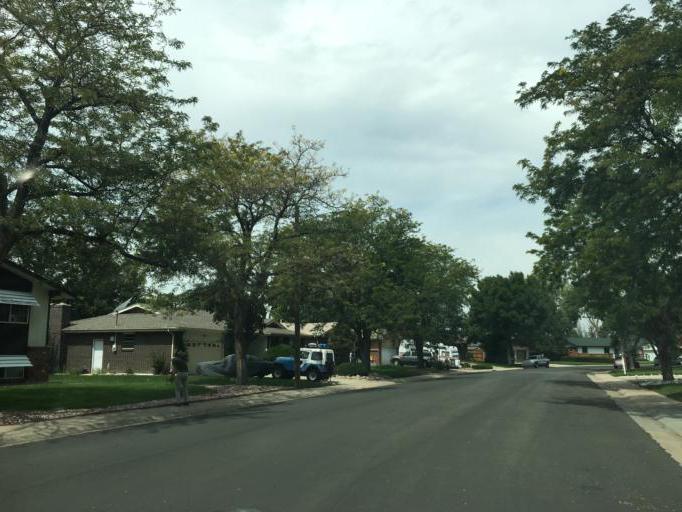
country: US
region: Colorado
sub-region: Adams County
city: Aurora
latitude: 39.7309
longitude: -104.8059
